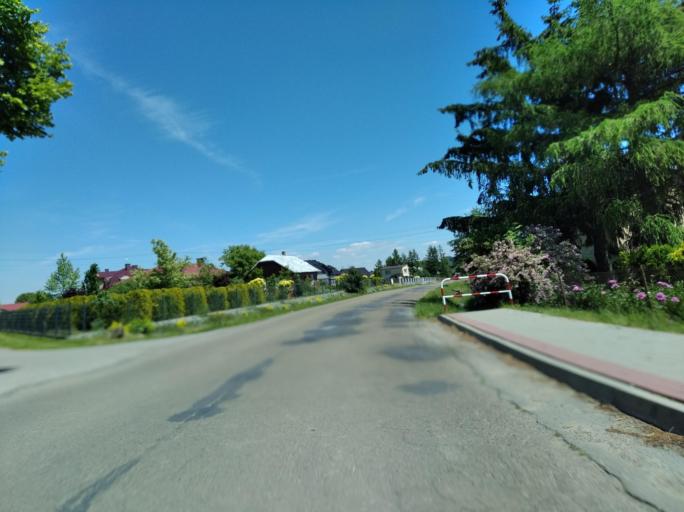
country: PL
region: Subcarpathian Voivodeship
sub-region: Powiat jasielski
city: Tarnowiec
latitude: 49.7179
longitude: 21.5563
